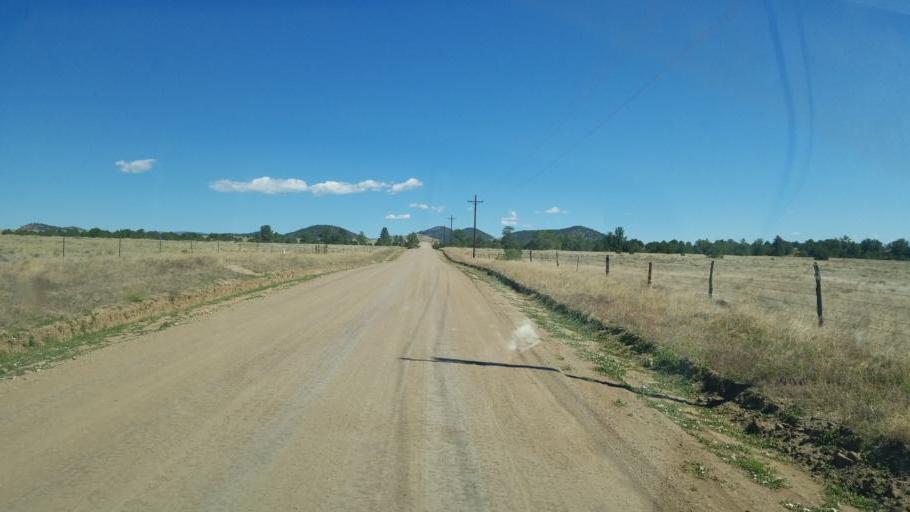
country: US
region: Colorado
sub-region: Custer County
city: Westcliffe
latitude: 38.2724
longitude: -105.5010
